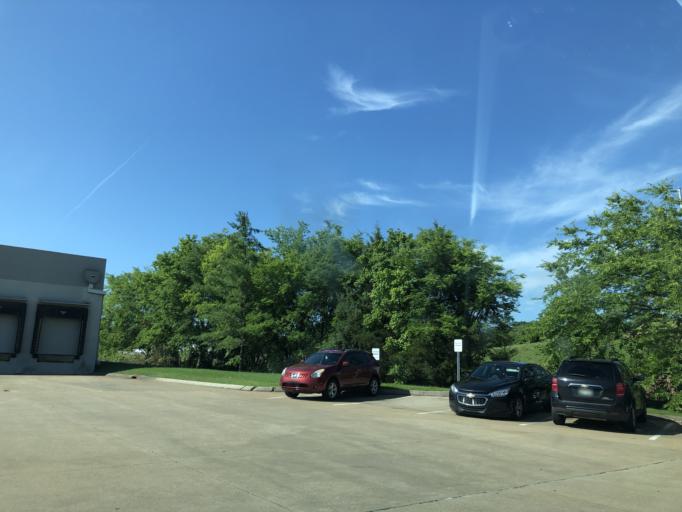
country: US
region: Tennessee
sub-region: Rutherford County
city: La Vergne
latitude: 36.0405
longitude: -86.6478
